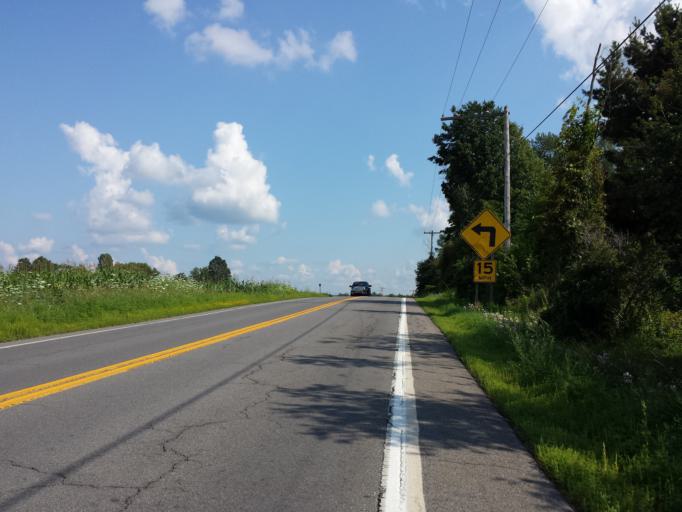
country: US
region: New York
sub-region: St. Lawrence County
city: Hannawa Falls
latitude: 44.6313
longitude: -74.9555
